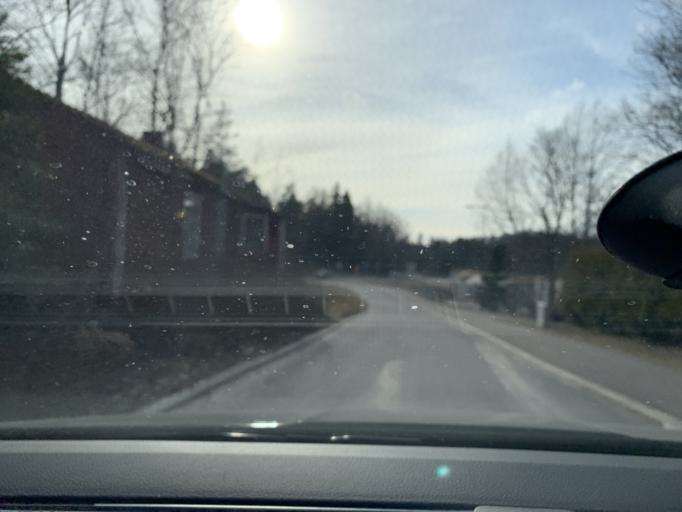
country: FI
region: Uusimaa
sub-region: Helsinki
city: Espoo
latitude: 60.1697
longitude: 24.6050
